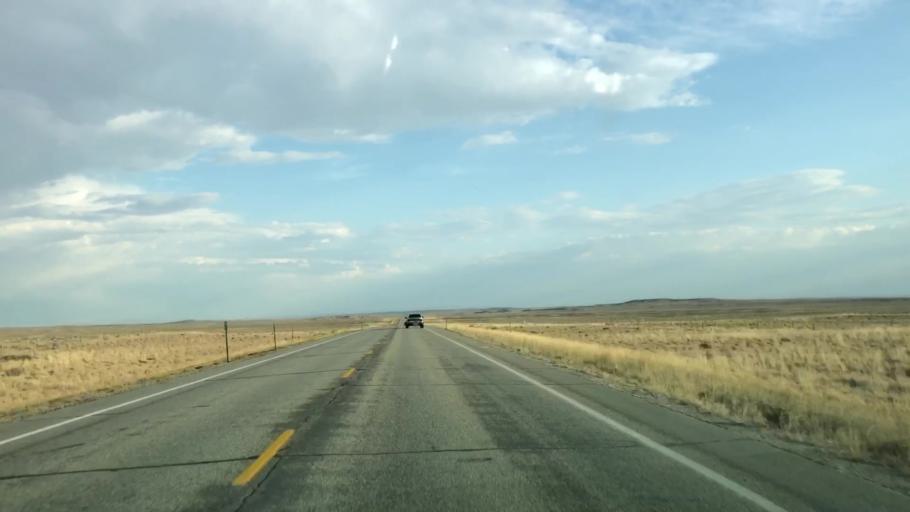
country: US
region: Wyoming
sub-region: Sublette County
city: Pinedale
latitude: 42.3883
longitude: -109.5390
